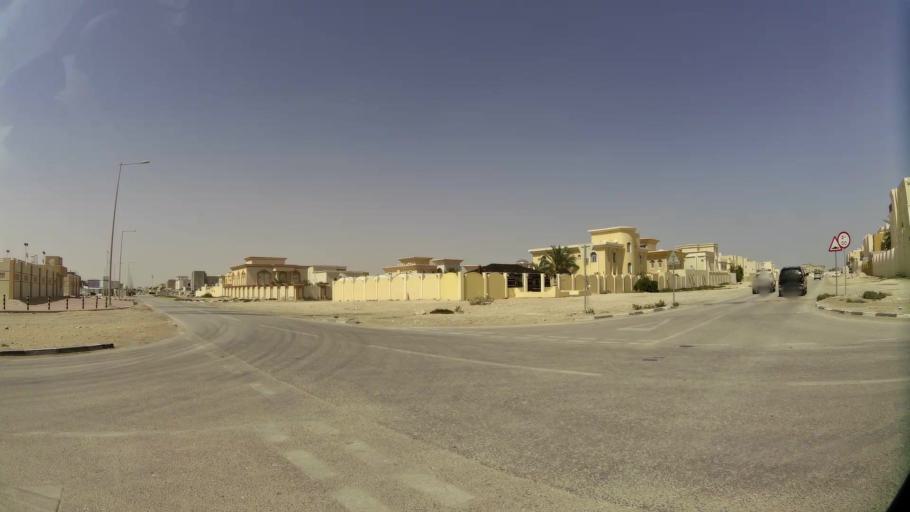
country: QA
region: Baladiyat Umm Salal
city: Umm Salal Muhammad
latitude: 25.3786
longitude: 51.4658
